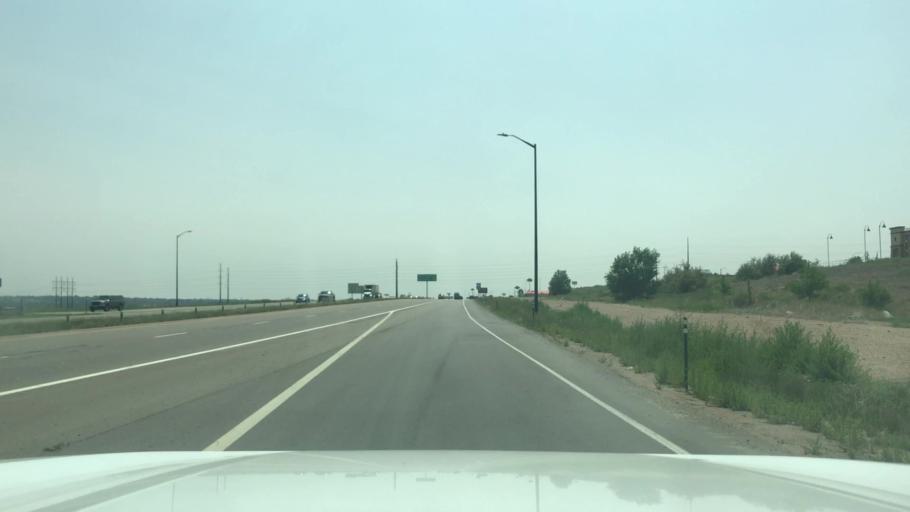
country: US
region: Colorado
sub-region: Pueblo County
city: Pueblo
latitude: 38.3356
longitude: -104.6193
